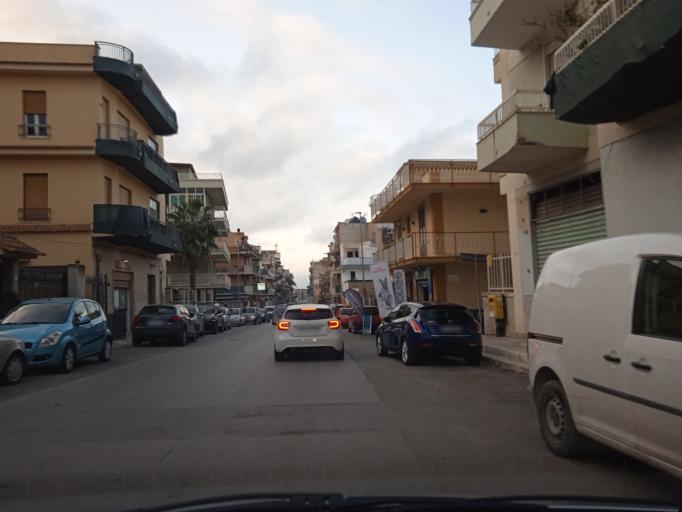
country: IT
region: Sicily
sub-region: Palermo
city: Villabate
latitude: 38.0785
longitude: 13.4378
